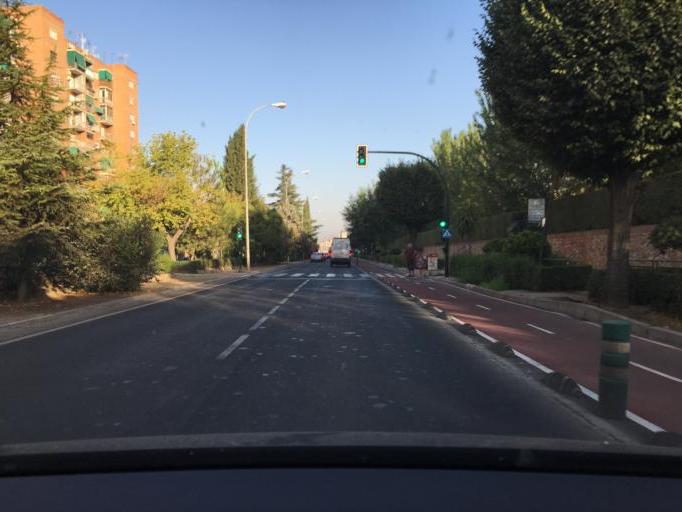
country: ES
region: Andalusia
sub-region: Provincia de Granada
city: Maracena
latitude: 37.1937
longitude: -3.6250
